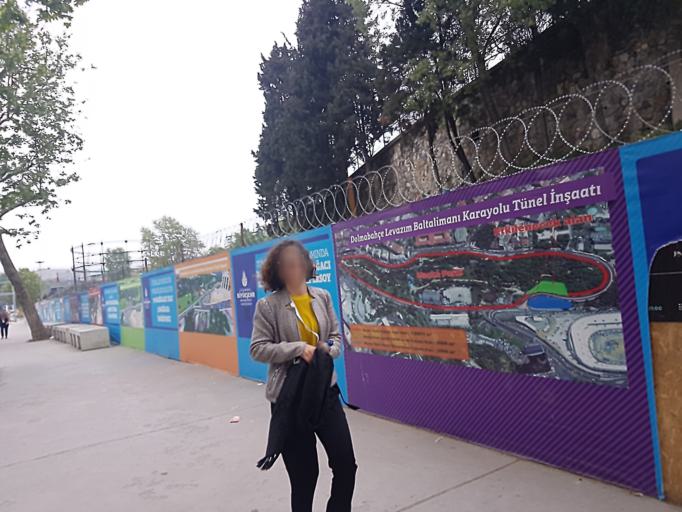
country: TR
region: Istanbul
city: Sisli
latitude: 41.0405
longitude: 28.9949
